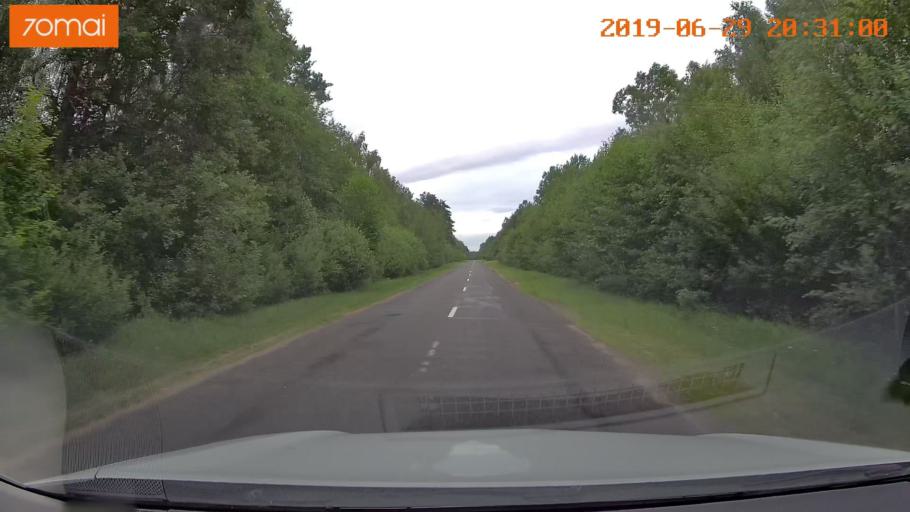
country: BY
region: Brest
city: Hantsavichy
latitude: 52.5104
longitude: 26.3369
